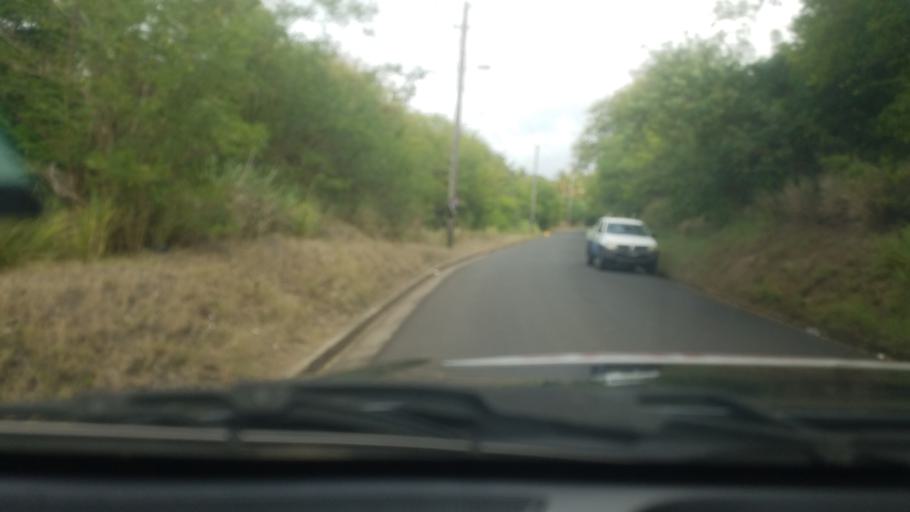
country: LC
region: Micoud Quarter
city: Micoud
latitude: 13.7955
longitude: -60.9086
